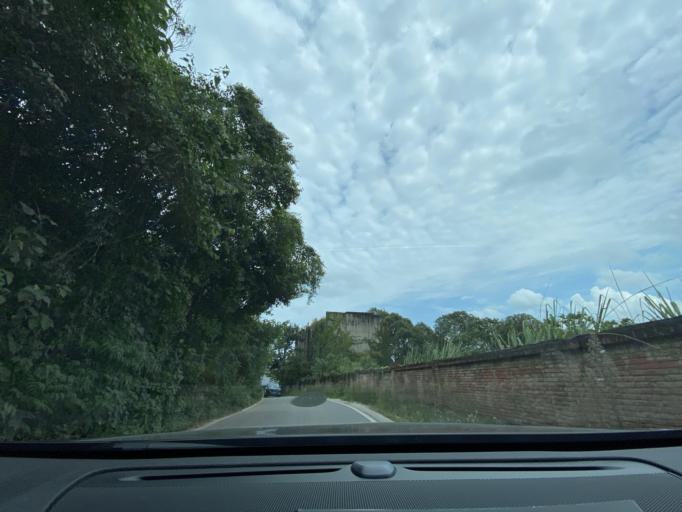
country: CN
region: Sichuan
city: Jiancheng
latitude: 30.4392
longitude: 104.5370
